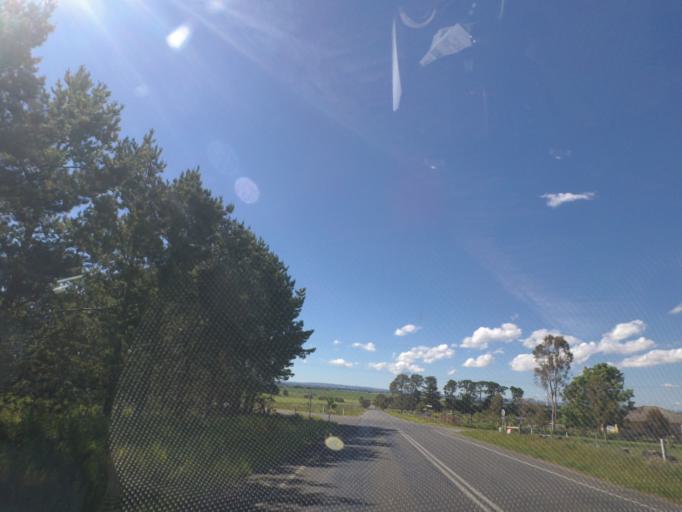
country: AU
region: Victoria
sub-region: Moorabool
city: Bacchus Marsh
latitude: -37.7453
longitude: 144.2218
